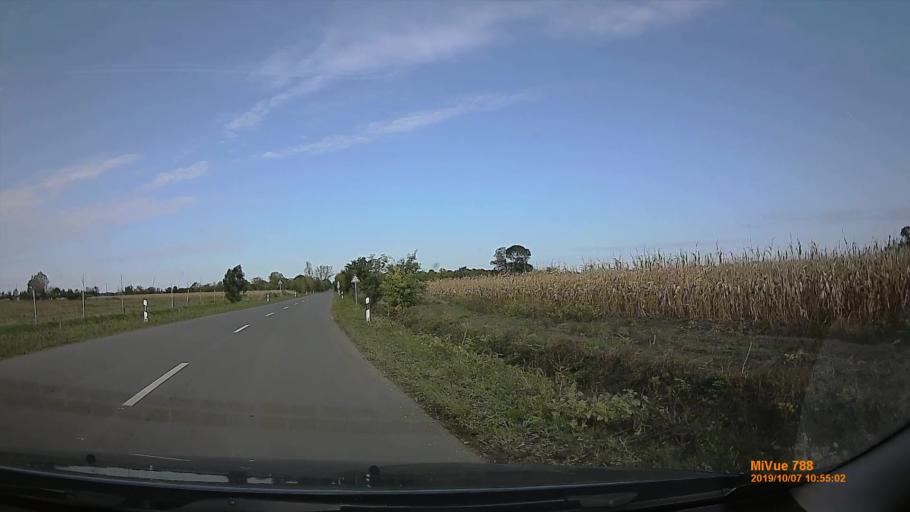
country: HU
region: Bekes
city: Kondoros
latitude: 46.7403
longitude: 20.8068
